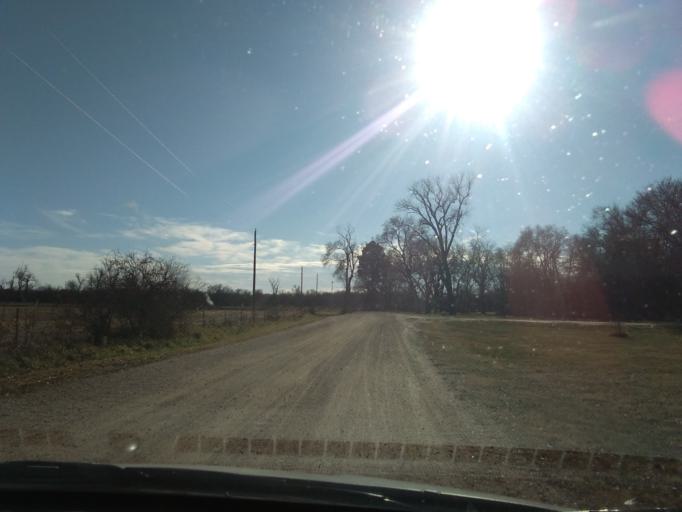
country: US
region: Nebraska
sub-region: Adams County
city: Hastings
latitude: 40.4540
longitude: -98.4419
